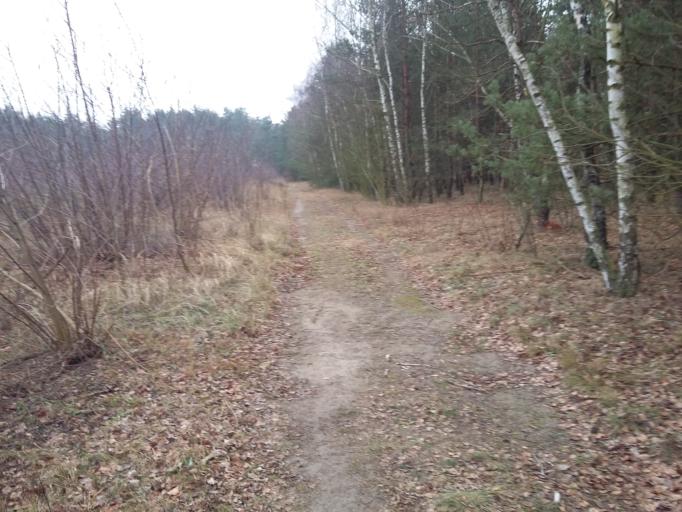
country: PL
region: Lodz Voivodeship
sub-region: Powiat pabianicki
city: Ksawerow
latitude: 51.7250
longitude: 19.3846
